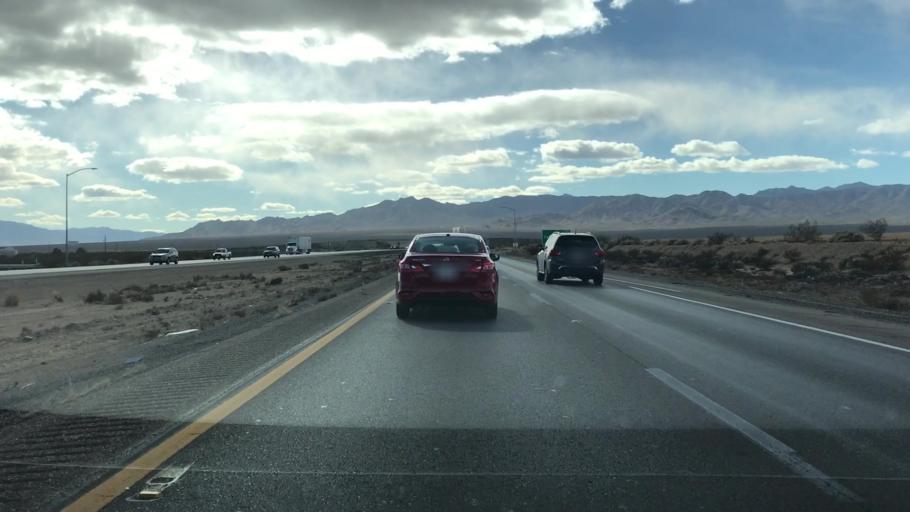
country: US
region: Nevada
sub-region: Clark County
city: Sandy Valley
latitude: 35.5463
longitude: -115.4174
